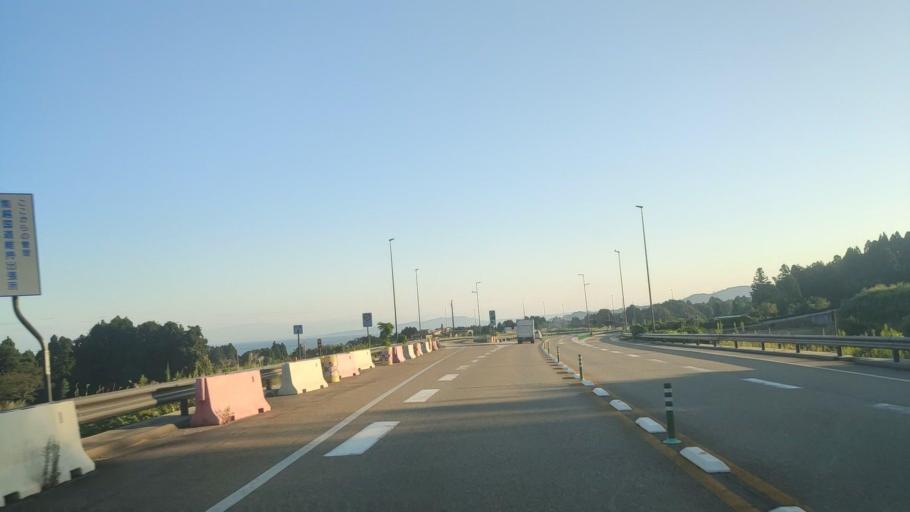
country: JP
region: Ishikawa
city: Nanao
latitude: 36.9640
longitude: 137.0484
